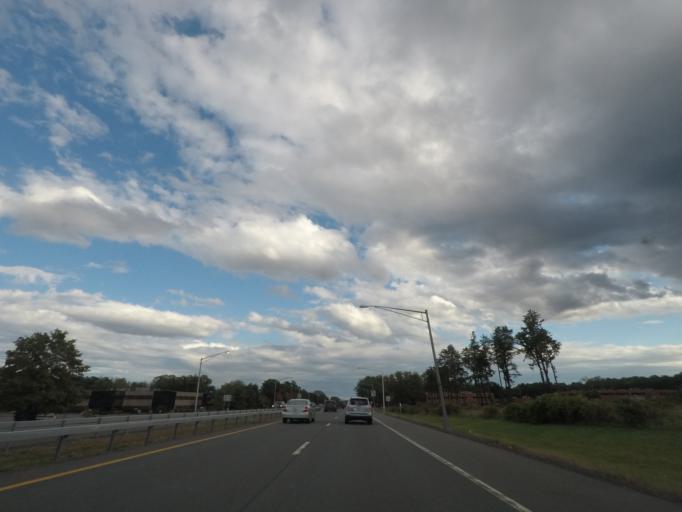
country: US
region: New York
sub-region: Albany County
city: Westmere
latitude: 42.7110
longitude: -73.8688
